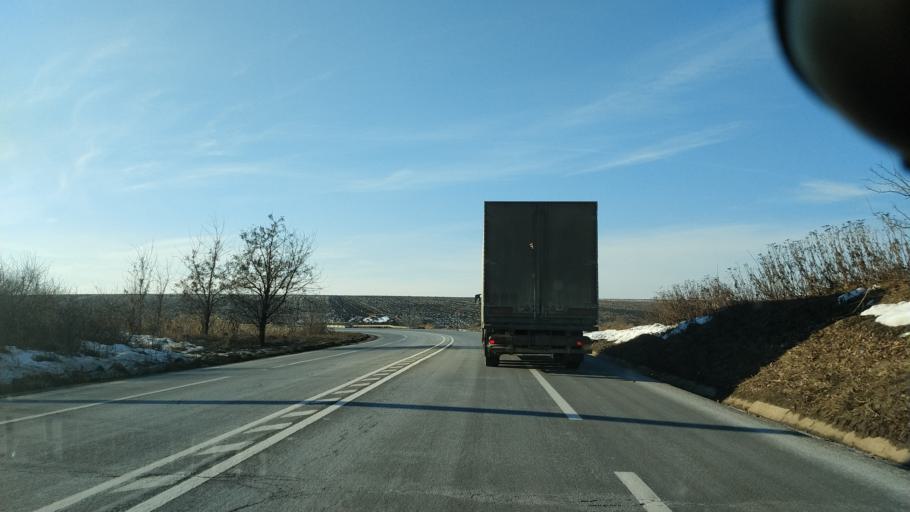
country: RO
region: Iasi
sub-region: Comuna Butea
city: Butea
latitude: 47.1108
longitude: 26.9287
